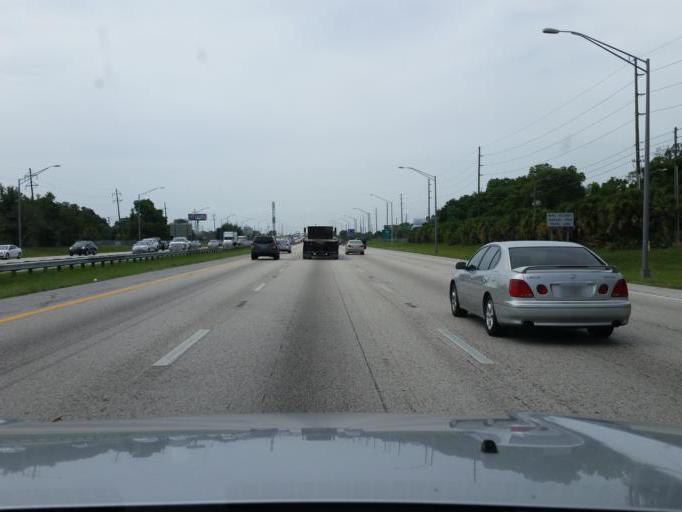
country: US
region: Florida
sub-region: Orange County
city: Eatonville
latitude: 28.6242
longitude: -81.3867
